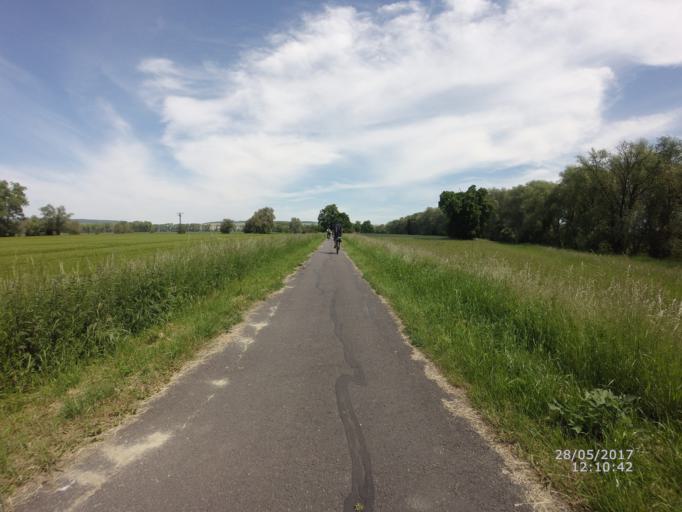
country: DE
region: Thuringia
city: Etzleben
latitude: 51.2584
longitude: 11.1674
